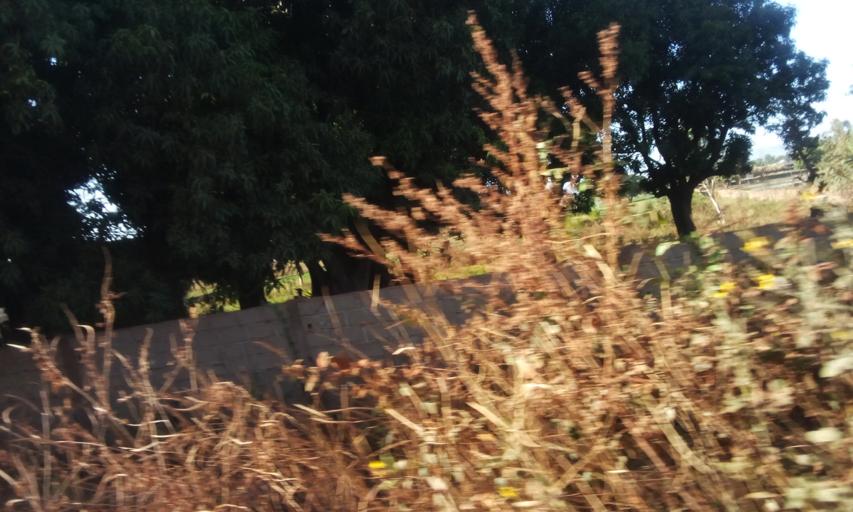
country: ML
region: Bamako
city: Bamako
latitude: 12.6419
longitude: -7.9075
